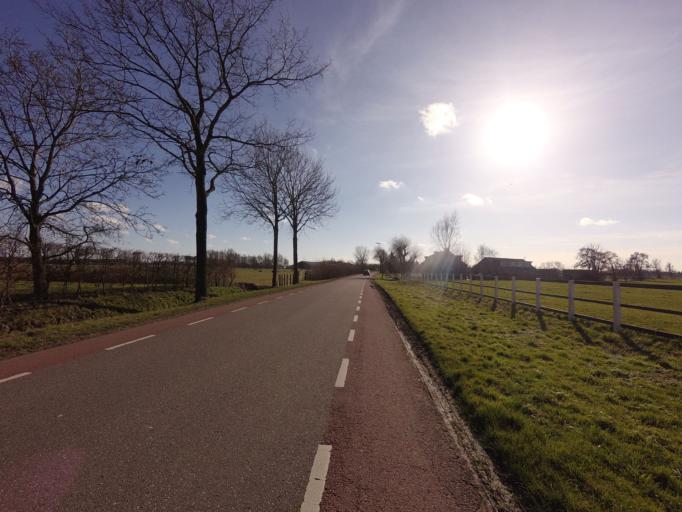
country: NL
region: Utrecht
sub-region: Gemeente Montfoort
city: Montfoort
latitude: 52.0607
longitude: 4.9616
